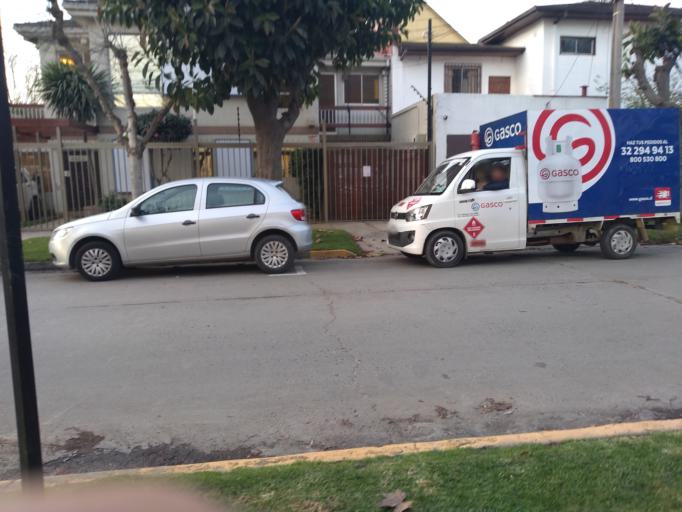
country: CL
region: Valparaiso
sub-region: Provincia de Valparaiso
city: Vina del Mar
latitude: -33.0219
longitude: -71.5421
